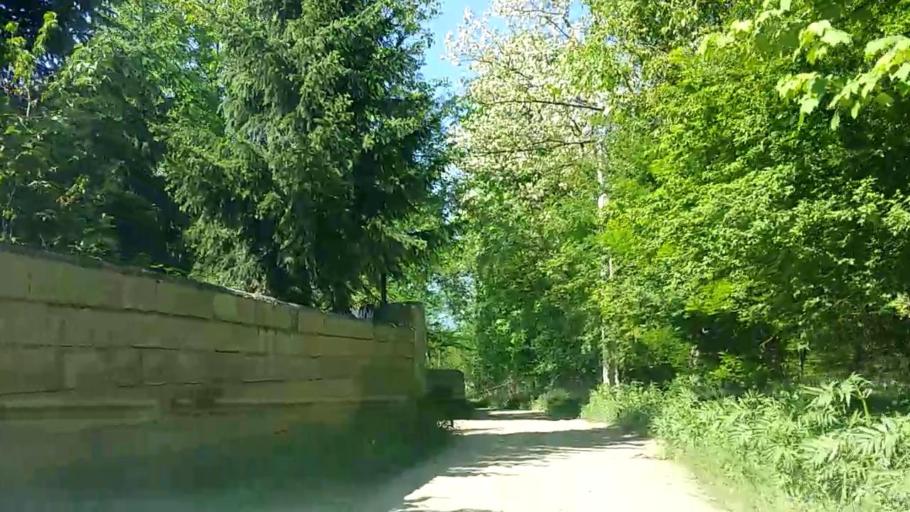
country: IR
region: Mazandaran
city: `Abbasabad
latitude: 36.5101
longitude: 51.1896
